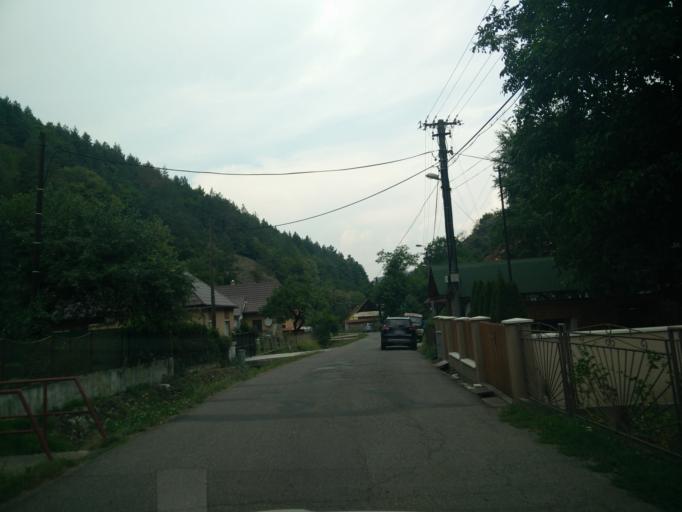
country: SK
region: Banskobystricky
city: Ziar nad Hronom
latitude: 48.5772
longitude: 18.8981
